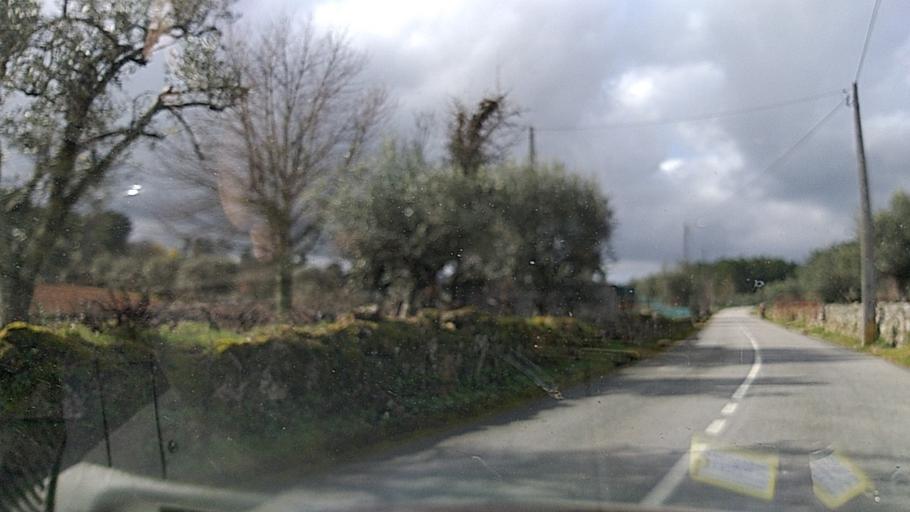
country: PT
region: Guarda
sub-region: Fornos de Algodres
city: Fornos de Algodres
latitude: 40.6626
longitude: -7.5724
